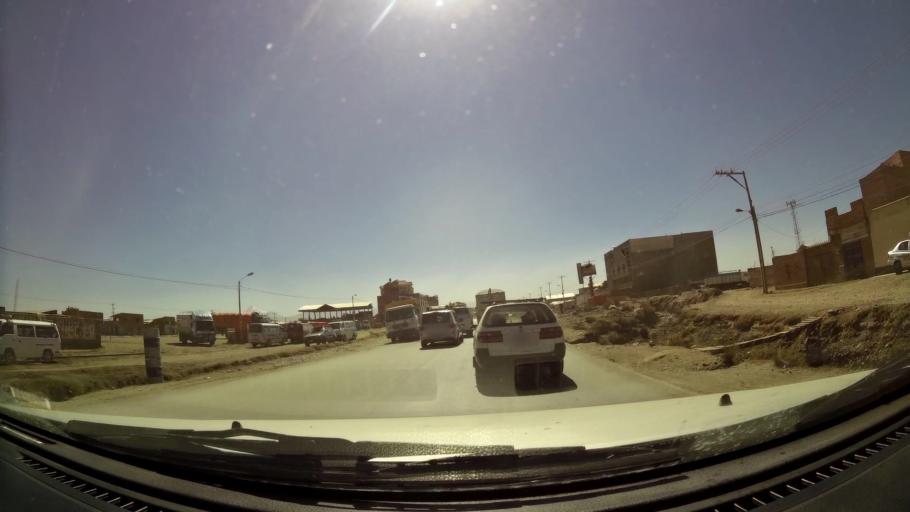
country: BO
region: La Paz
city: La Paz
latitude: -16.5609
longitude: -68.2150
